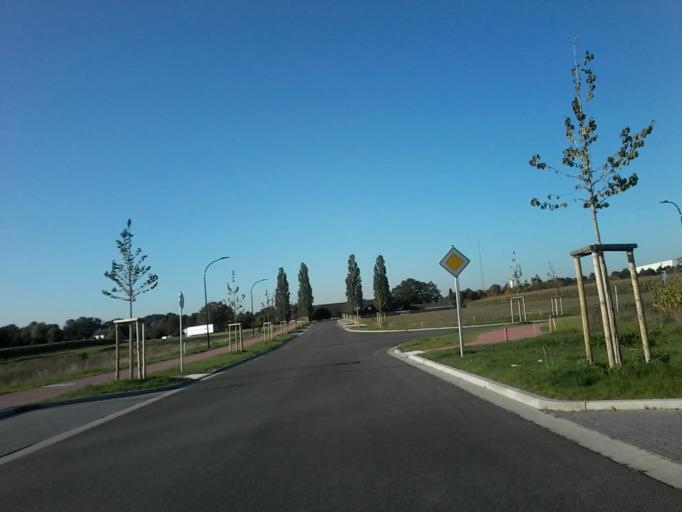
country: DE
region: Lower Saxony
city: Oyten
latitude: 53.0490
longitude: 9.0363
